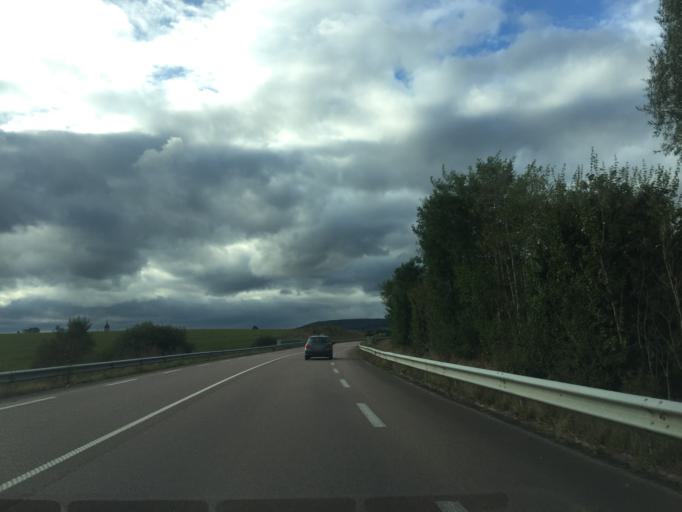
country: FR
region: Lorraine
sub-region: Departement des Vosges
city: Chatenois
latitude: 48.2922
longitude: 5.8951
